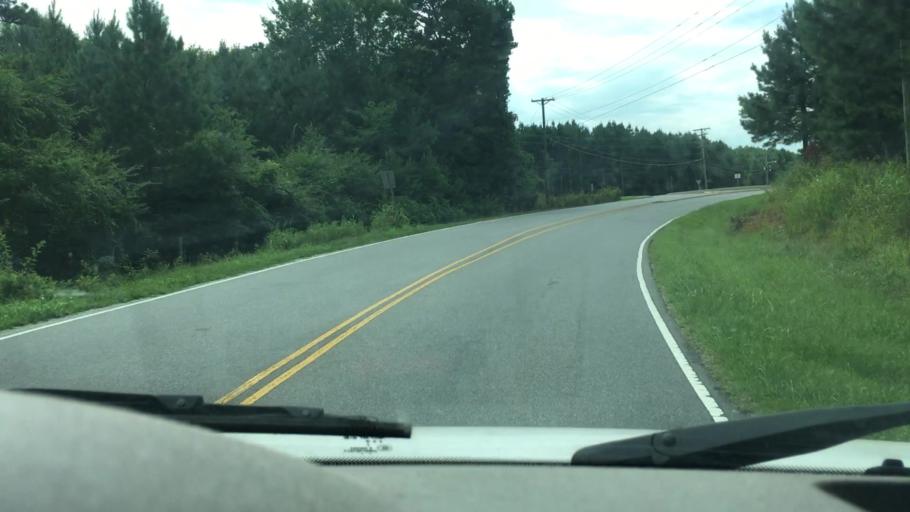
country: US
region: North Carolina
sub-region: Gaston County
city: Davidson
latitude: 35.4835
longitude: -80.8186
